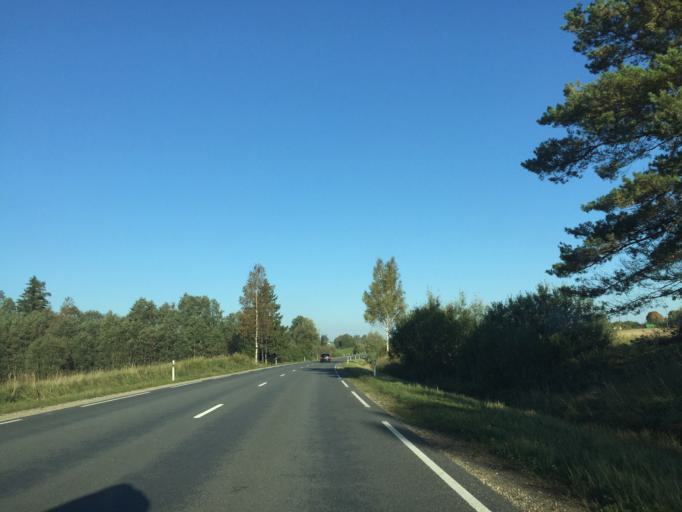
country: LV
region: Raunas
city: Rauna
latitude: 57.2622
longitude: 25.5280
